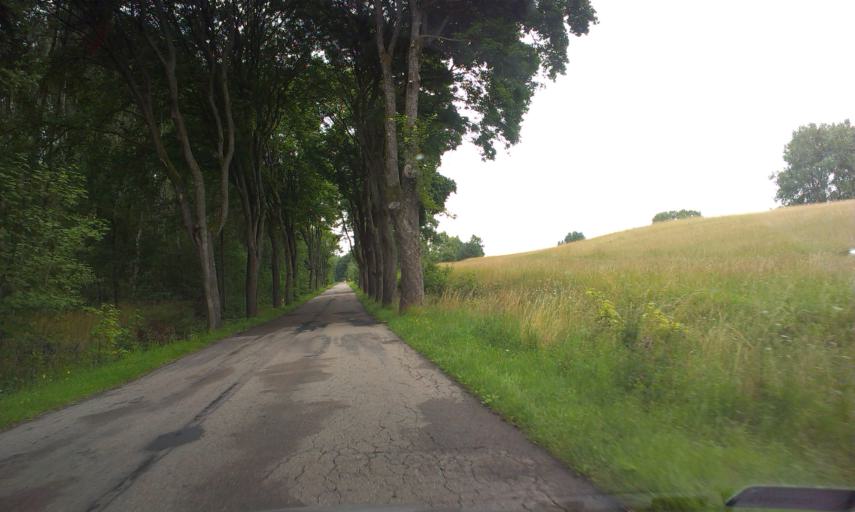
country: PL
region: West Pomeranian Voivodeship
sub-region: Powiat szczecinecki
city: Barwice
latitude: 53.6732
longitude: 16.3427
